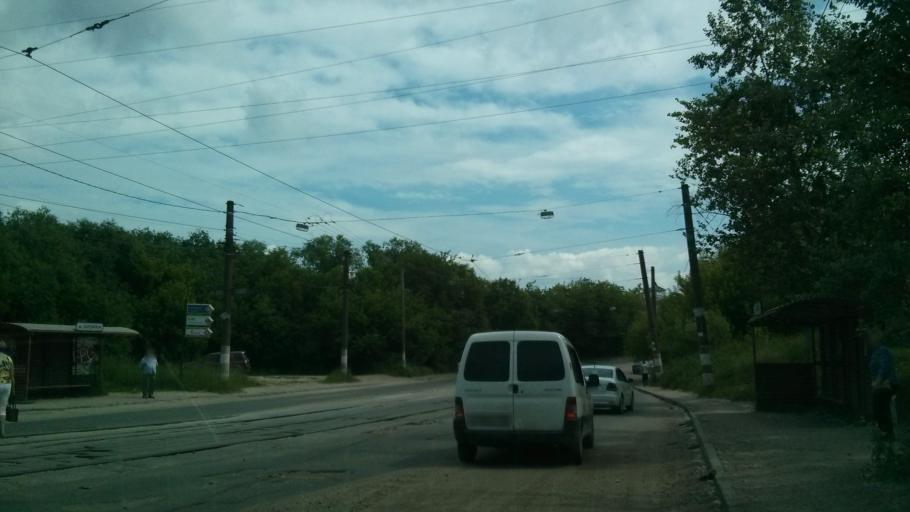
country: RU
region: Nizjnij Novgorod
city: Nizhniy Novgorod
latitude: 56.3051
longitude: 44.0219
